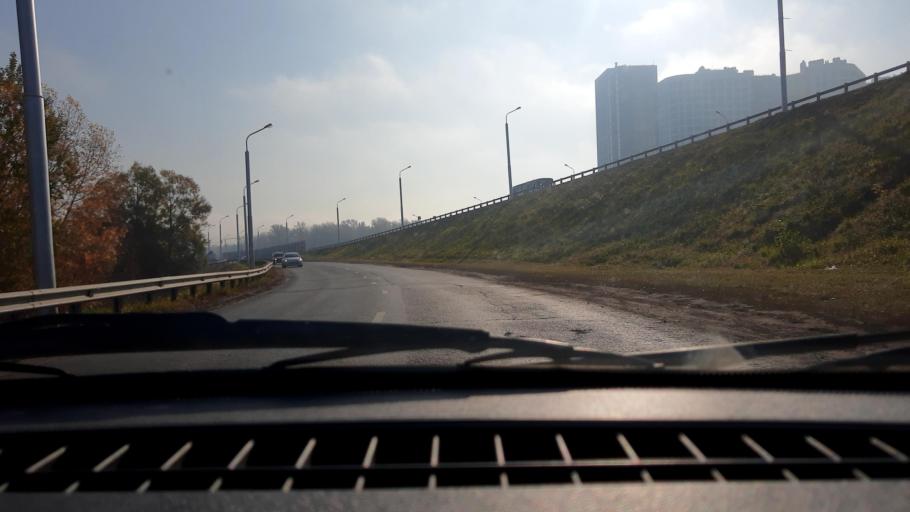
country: RU
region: Bashkortostan
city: Mikhaylovka
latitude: 54.7017
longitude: 55.8612
